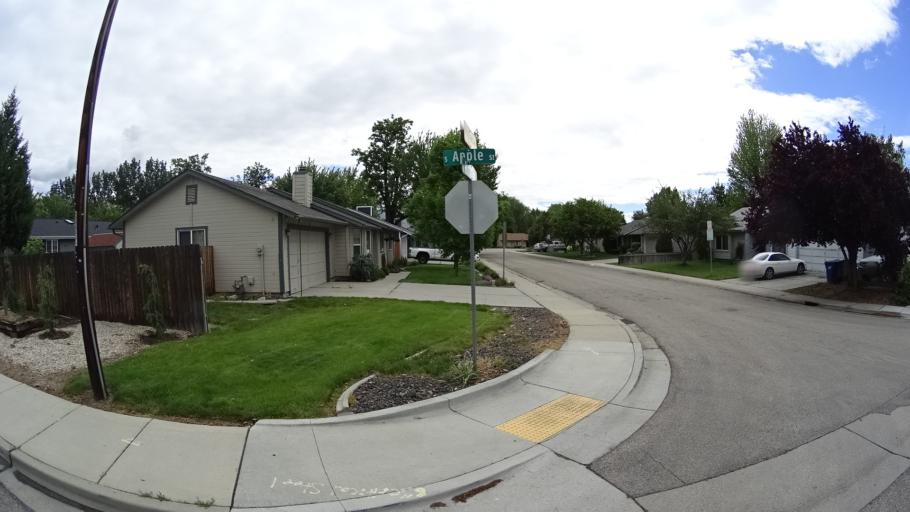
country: US
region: Idaho
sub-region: Ada County
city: Boise
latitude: 43.5769
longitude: -116.1733
